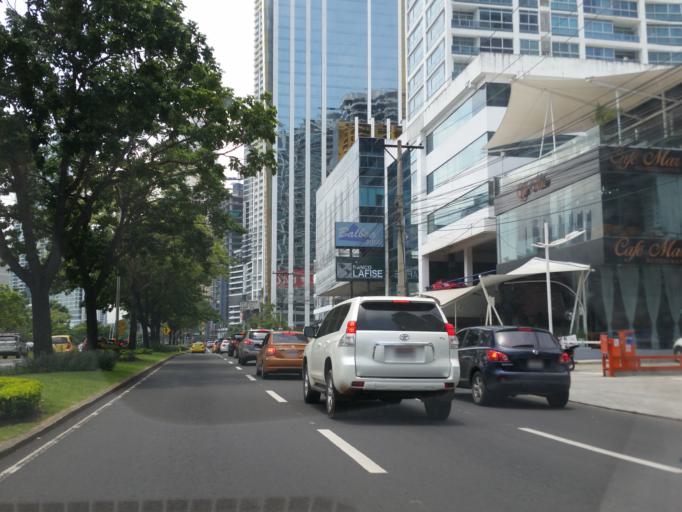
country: PA
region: Panama
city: Panama
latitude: 8.9757
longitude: -79.5206
